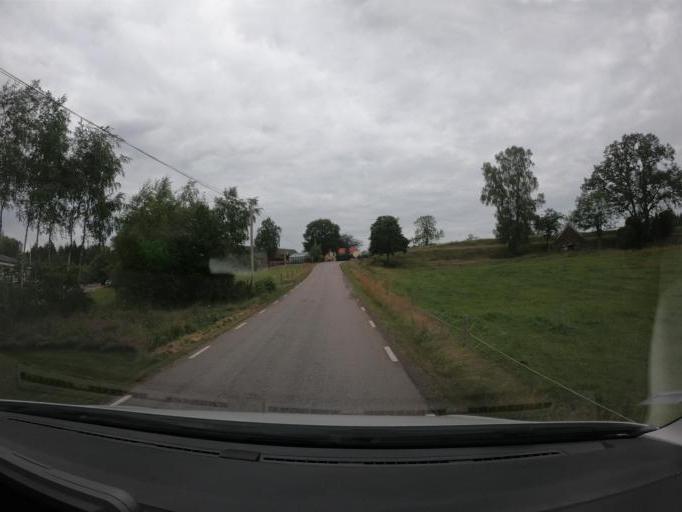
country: SE
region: Skane
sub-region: Orkelljunga Kommun
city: OErkelljunga
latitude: 56.2633
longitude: 13.1541
